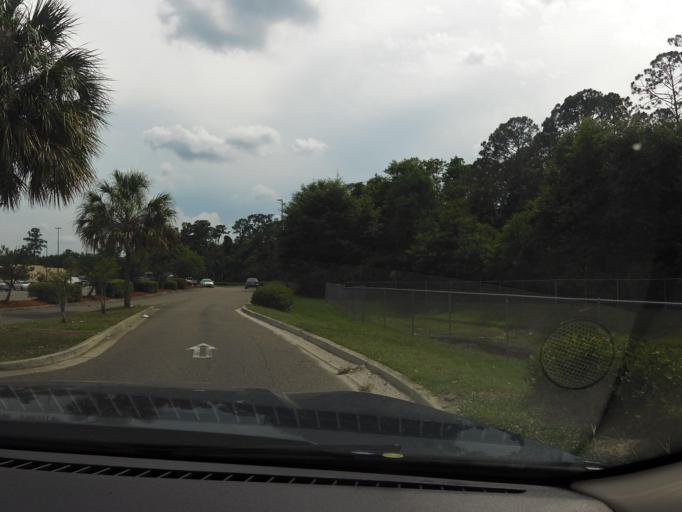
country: US
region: Florida
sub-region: Baker County
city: Macclenny
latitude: 30.2650
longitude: -82.1092
